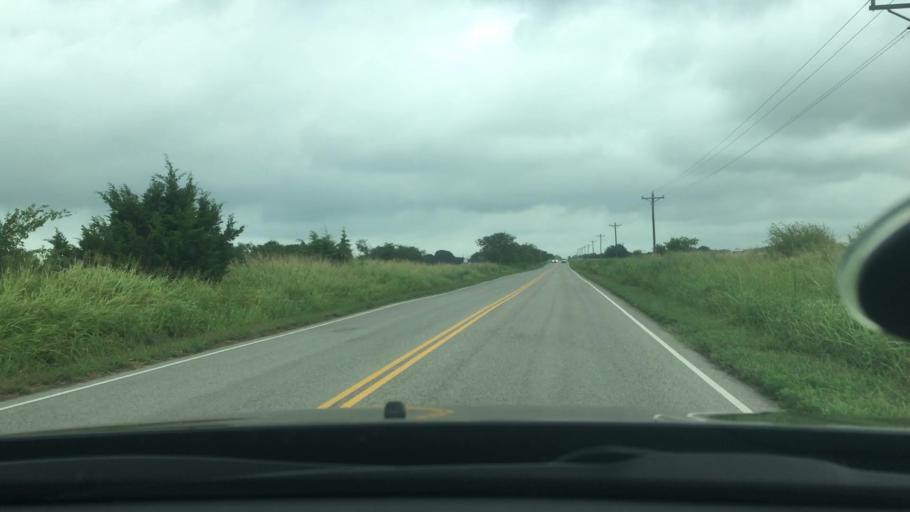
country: US
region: Oklahoma
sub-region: Bryan County
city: Calera
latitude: 33.9292
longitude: -96.5005
